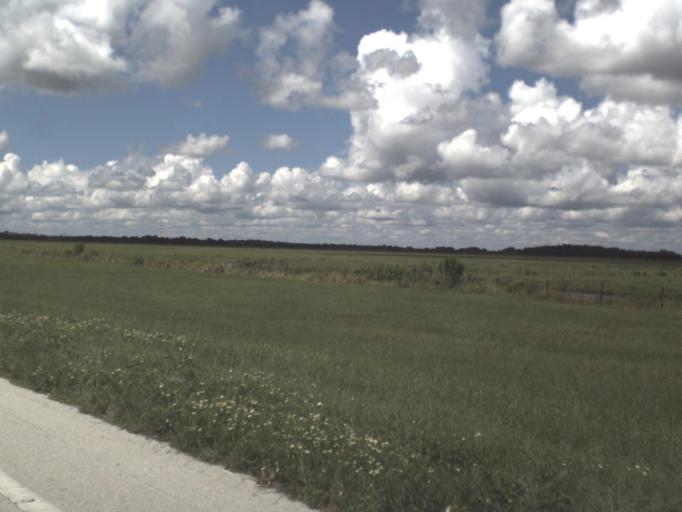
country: US
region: Florida
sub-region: DeSoto County
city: Southeast Arcadia
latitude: 27.2094
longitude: -81.7337
